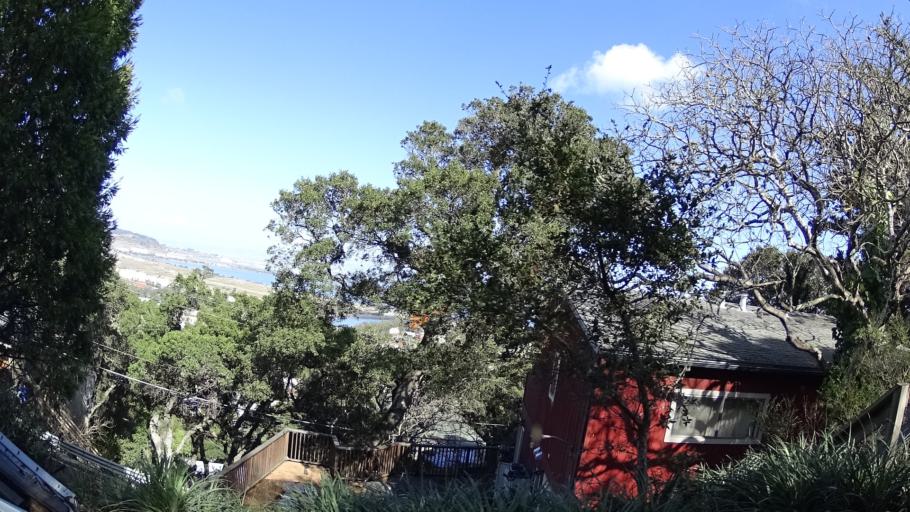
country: US
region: California
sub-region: San Mateo County
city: Brisbane
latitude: 37.6793
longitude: -122.4062
